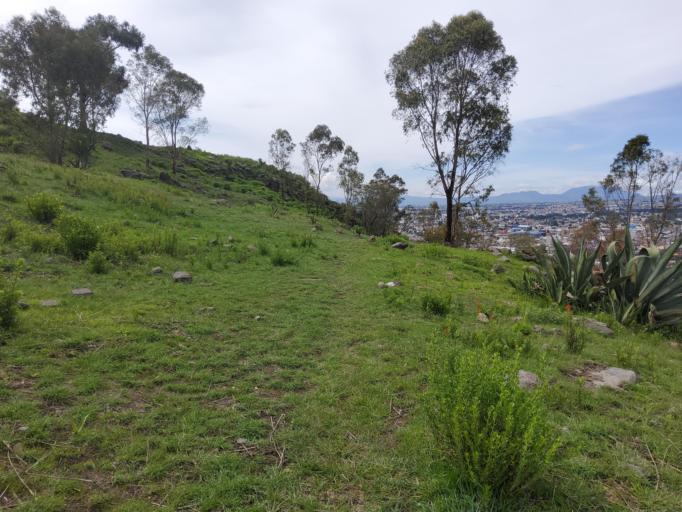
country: MX
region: Mexico
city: Toluca
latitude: 19.3033
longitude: -99.6588
